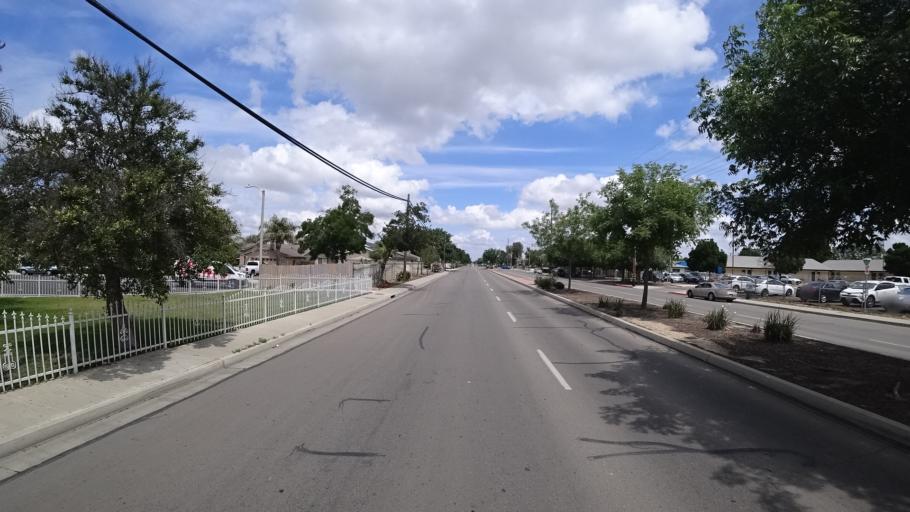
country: US
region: California
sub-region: Kings County
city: Home Garden
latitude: 36.3075
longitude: -119.6551
